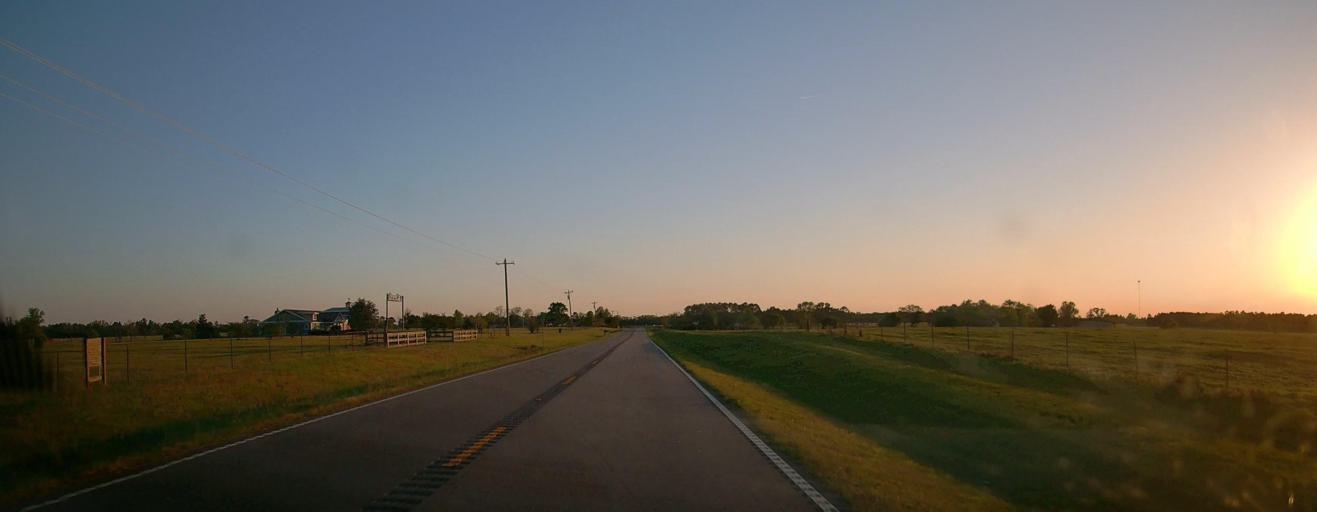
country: US
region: Georgia
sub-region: Marion County
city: Buena Vista
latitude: 32.4883
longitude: -84.6206
